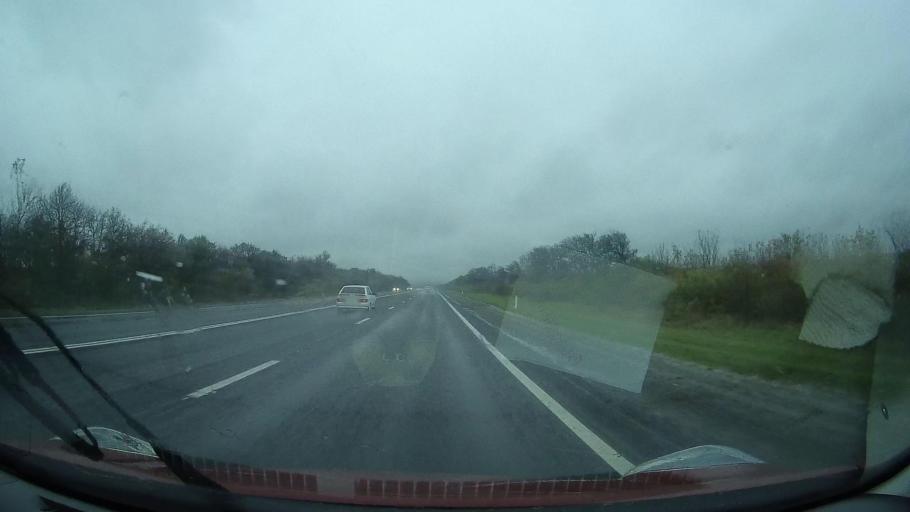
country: RU
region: Stavropol'skiy
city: Nevinnomyssk
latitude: 44.6174
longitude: 42.1009
